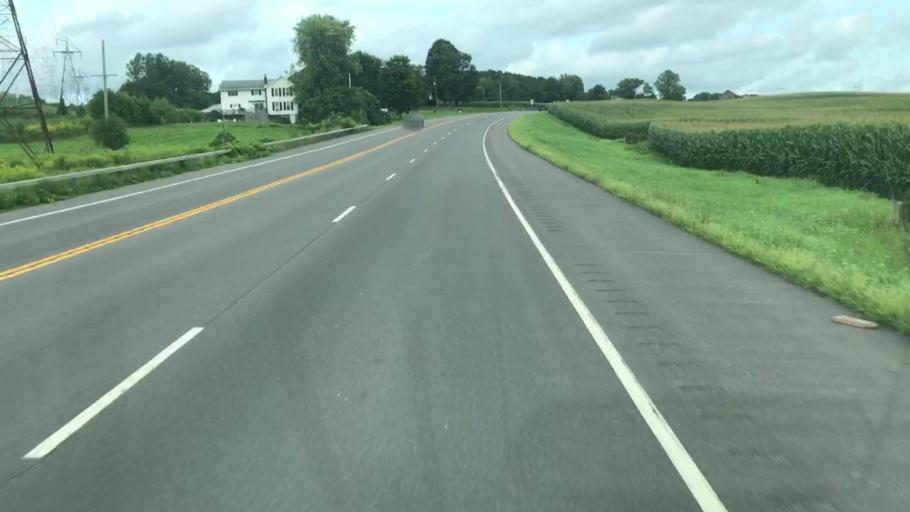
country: US
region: New York
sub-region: Onondaga County
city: Peru
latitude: 43.0376
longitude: -76.3997
